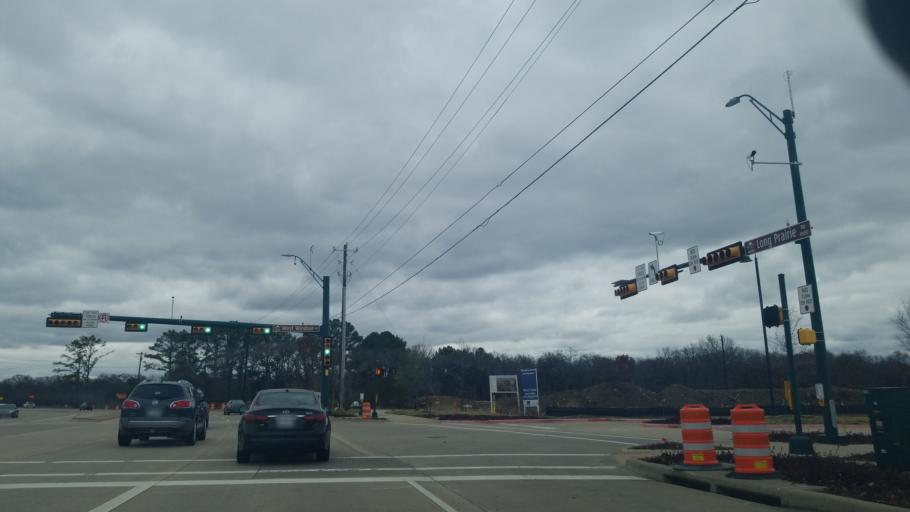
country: US
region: Texas
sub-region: Denton County
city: Flower Mound
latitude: 33.0472
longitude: -97.0694
